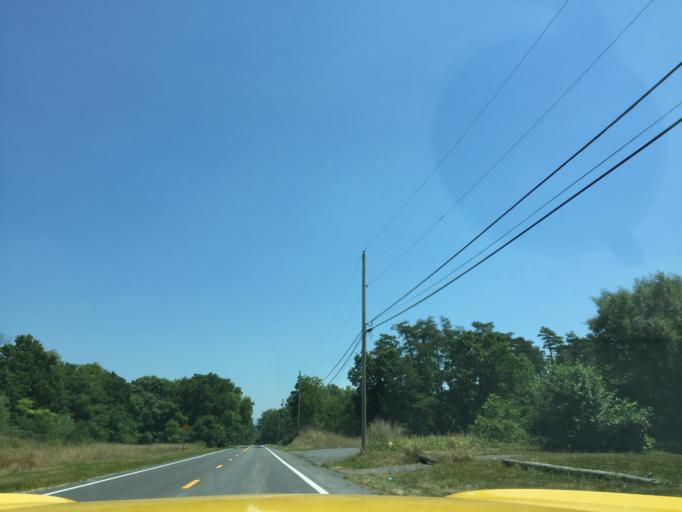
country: US
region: West Virginia
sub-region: Berkeley County
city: Inwood
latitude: 39.3239
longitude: -77.9980
